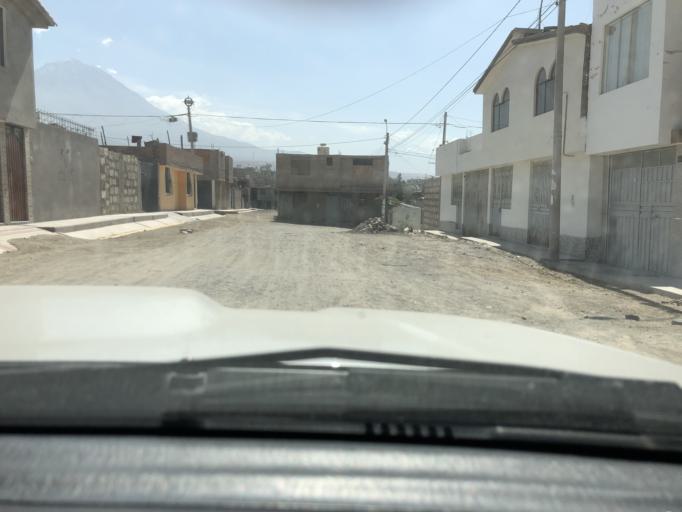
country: PE
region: Arequipa
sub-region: Provincia de Arequipa
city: Arequipa
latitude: -16.3406
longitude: -71.5507
